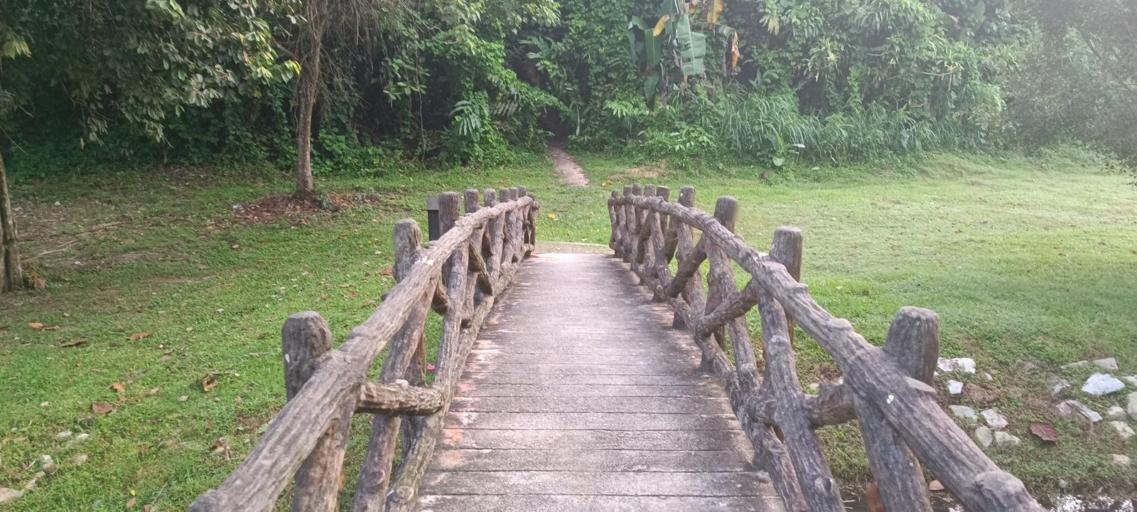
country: MY
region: Penang
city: Tanjung Tokong
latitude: 5.4360
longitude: 100.2930
